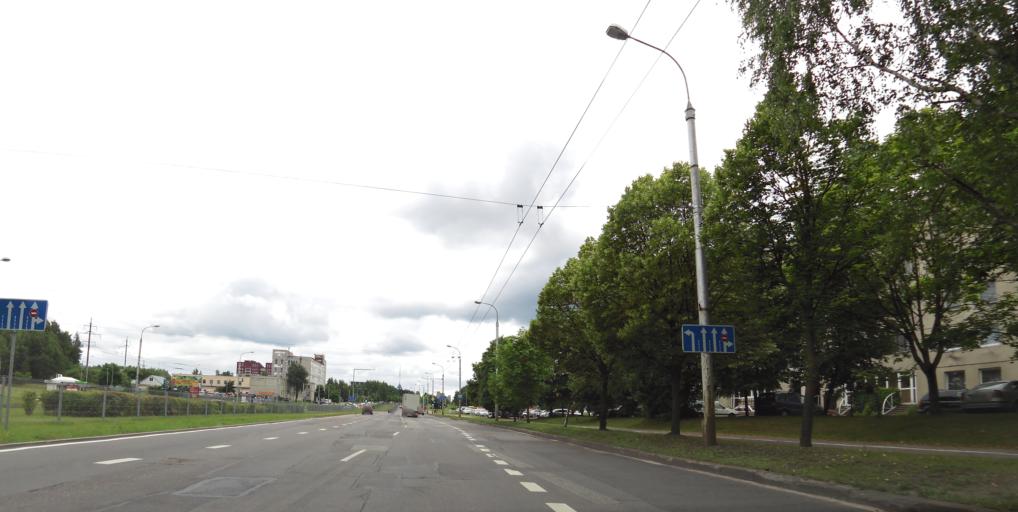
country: LT
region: Vilnius County
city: Justiniskes
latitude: 54.7176
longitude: 25.2314
